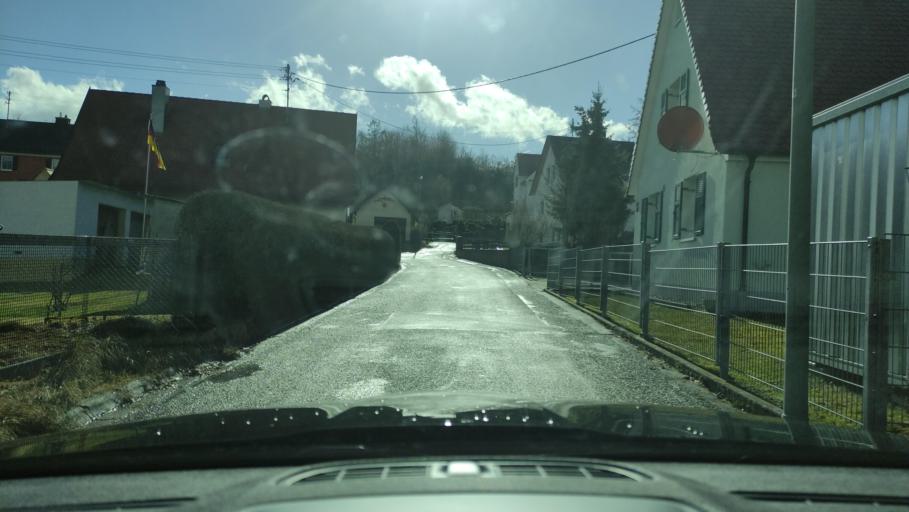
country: DE
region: Bavaria
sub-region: Swabia
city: Krumbach
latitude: 48.2525
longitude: 10.3504
